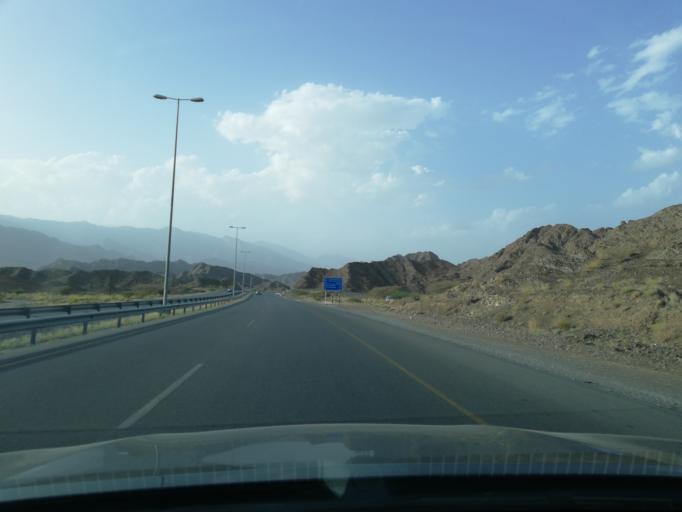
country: OM
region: Muhafazat ad Dakhiliyah
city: Izki
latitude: 22.9394
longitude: 57.7905
